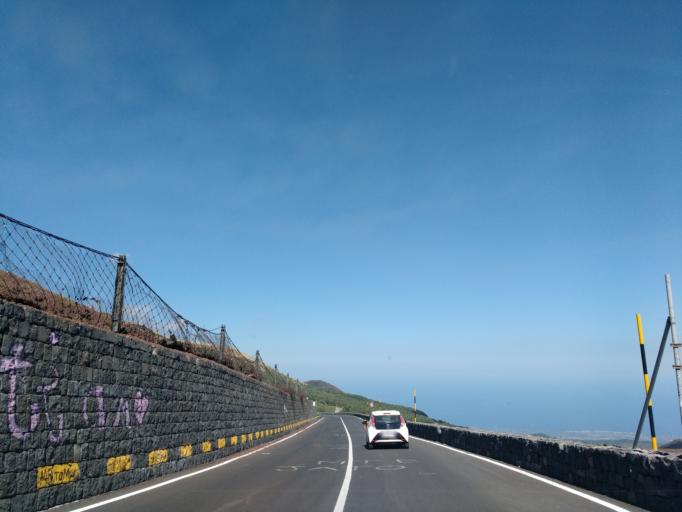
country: IT
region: Sicily
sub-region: Catania
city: Nicolosi
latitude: 37.6989
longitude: 15.0059
